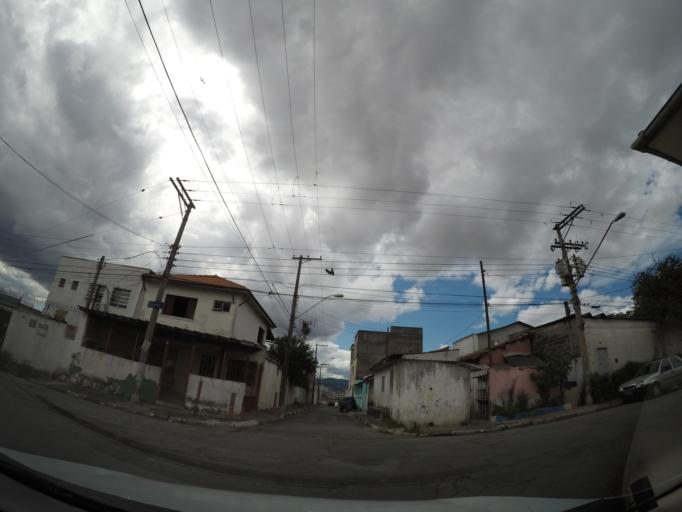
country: BR
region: Sao Paulo
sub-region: Guarulhos
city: Guarulhos
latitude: -23.4954
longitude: -46.5575
